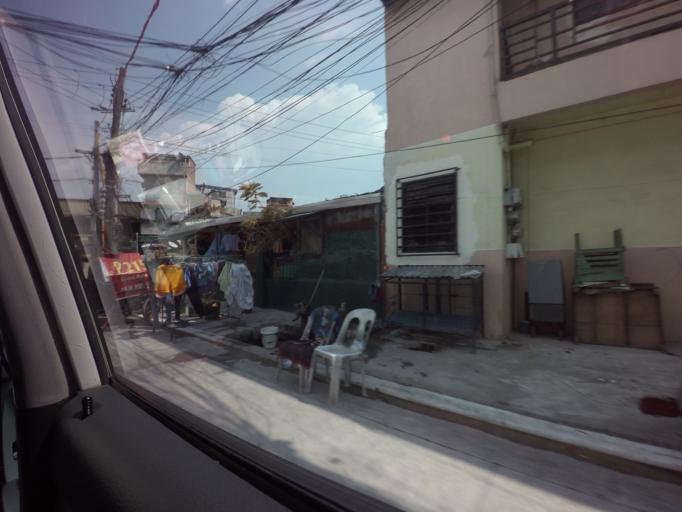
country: PH
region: Metro Manila
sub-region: San Juan
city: San Juan
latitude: 14.6009
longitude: 121.0095
